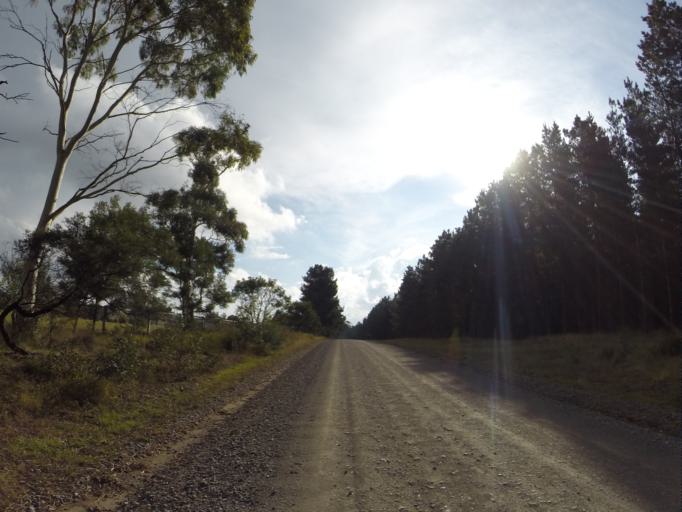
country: AU
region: New South Wales
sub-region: Wingecarribee
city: Bundanoon
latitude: -34.5341
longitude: 150.2293
